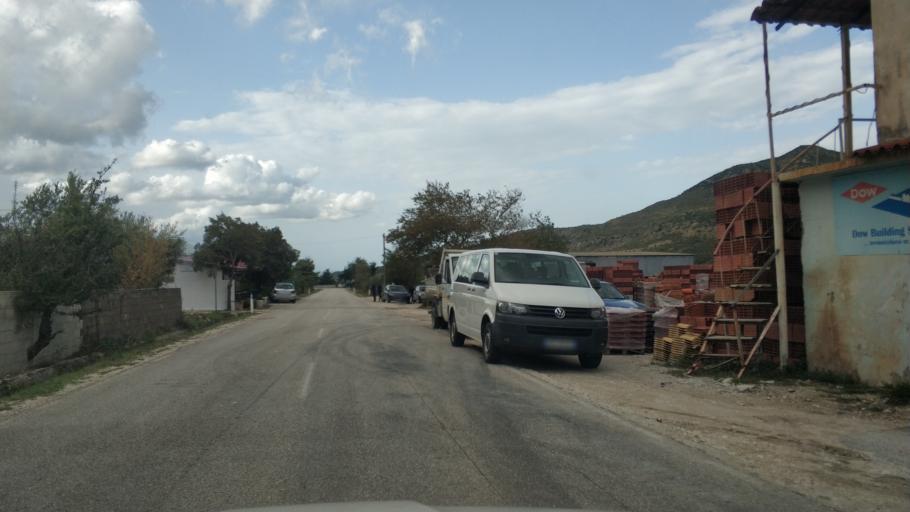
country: AL
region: Vlore
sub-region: Rrethi i Vlores
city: Orikum
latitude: 40.2701
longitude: 19.5139
